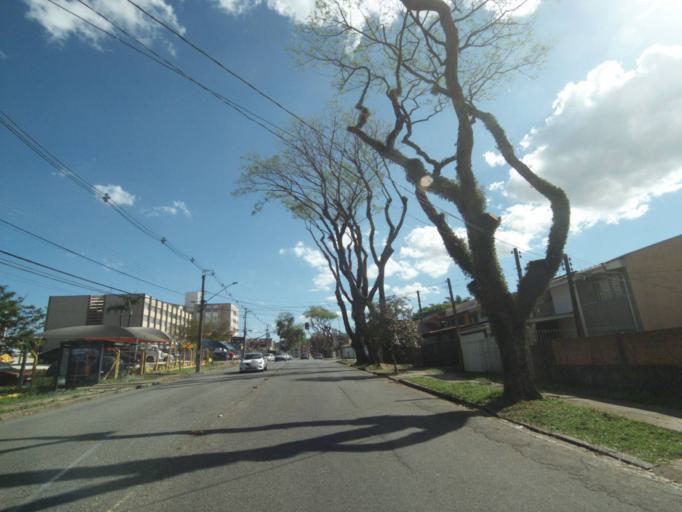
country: BR
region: Parana
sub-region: Curitiba
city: Curitiba
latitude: -25.3971
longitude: -49.2503
